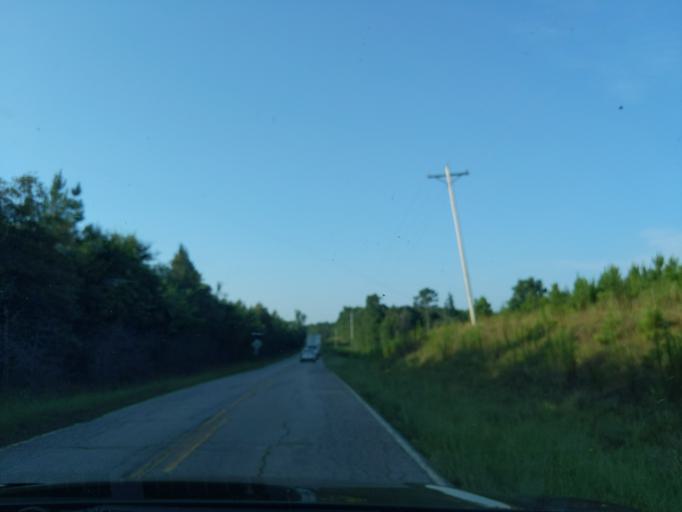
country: US
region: South Carolina
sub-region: Spartanburg County
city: Woodruff
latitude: 34.7924
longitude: -81.9725
